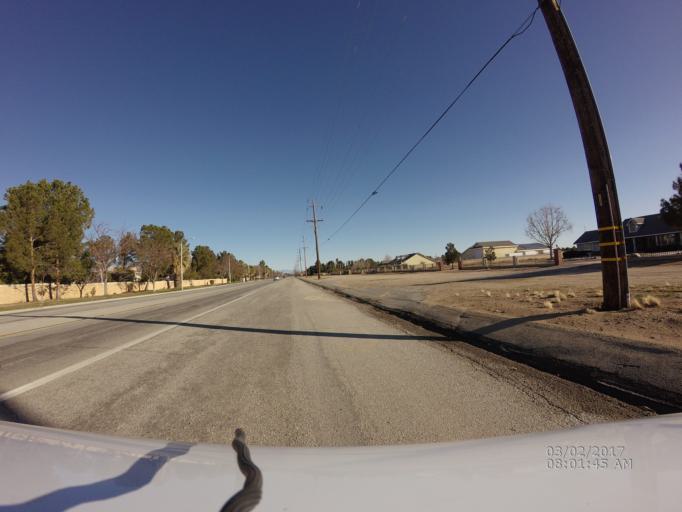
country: US
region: California
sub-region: Los Angeles County
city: Desert View Highlands
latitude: 34.6094
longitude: -118.1833
